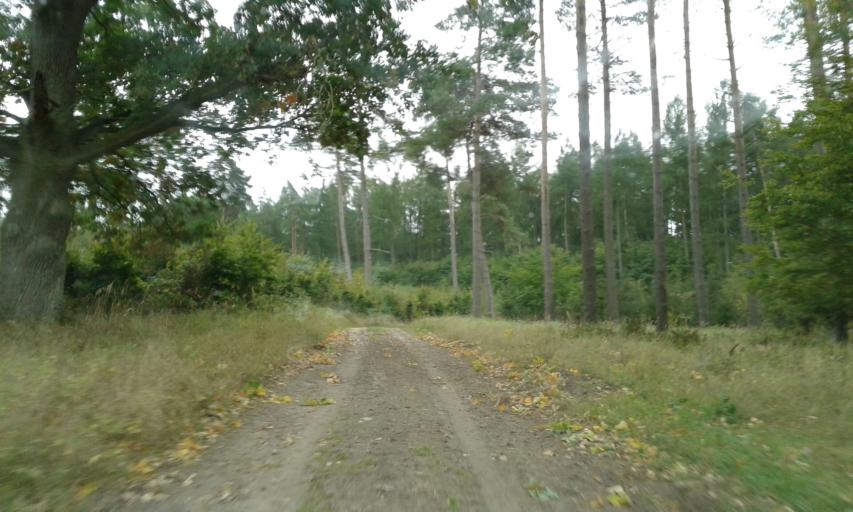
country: PL
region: West Pomeranian Voivodeship
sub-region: Powiat choszczenski
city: Pelczyce
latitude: 53.0859
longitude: 15.2522
